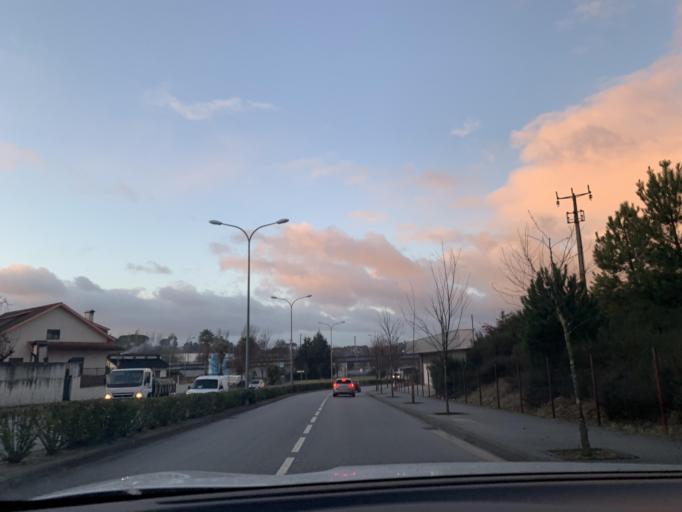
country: PT
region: Viseu
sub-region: Viseu
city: Viseu
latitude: 40.6241
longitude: -7.9168
